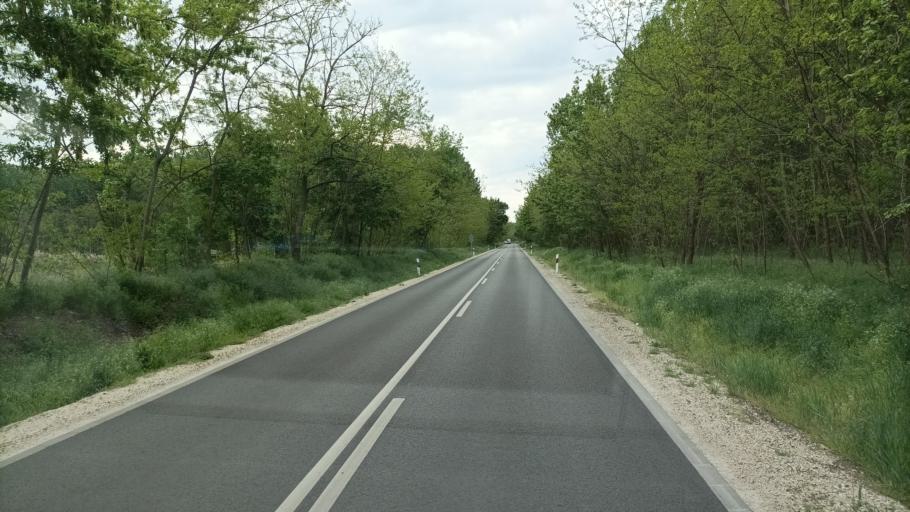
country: HU
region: Pest
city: Nyaregyhaza
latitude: 47.2862
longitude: 19.4577
